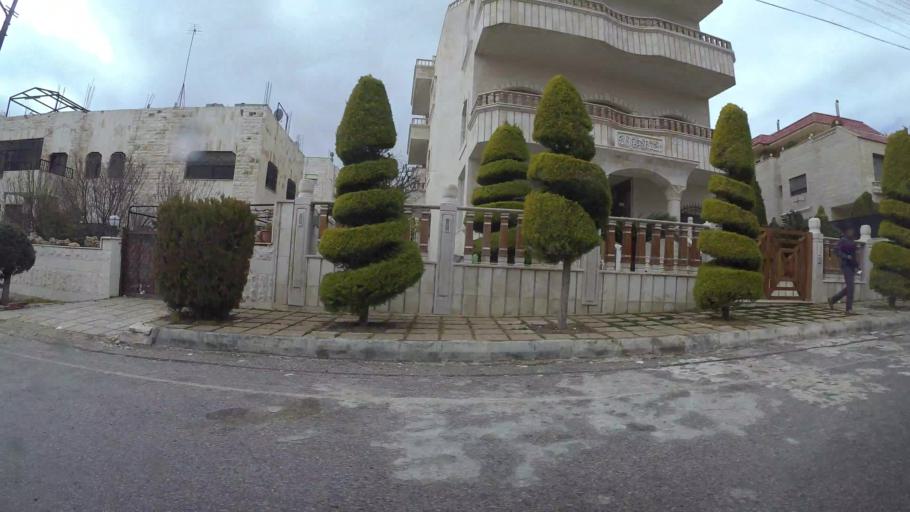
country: JO
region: Amman
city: Al Jubayhah
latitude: 31.9885
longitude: 35.8599
